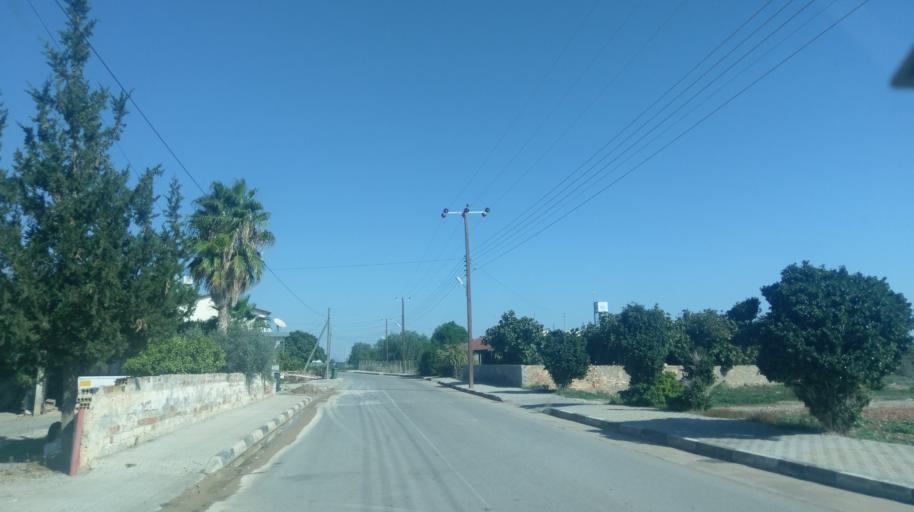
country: CY
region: Ammochostos
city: Lefkonoiko
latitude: 35.2418
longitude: 33.7807
